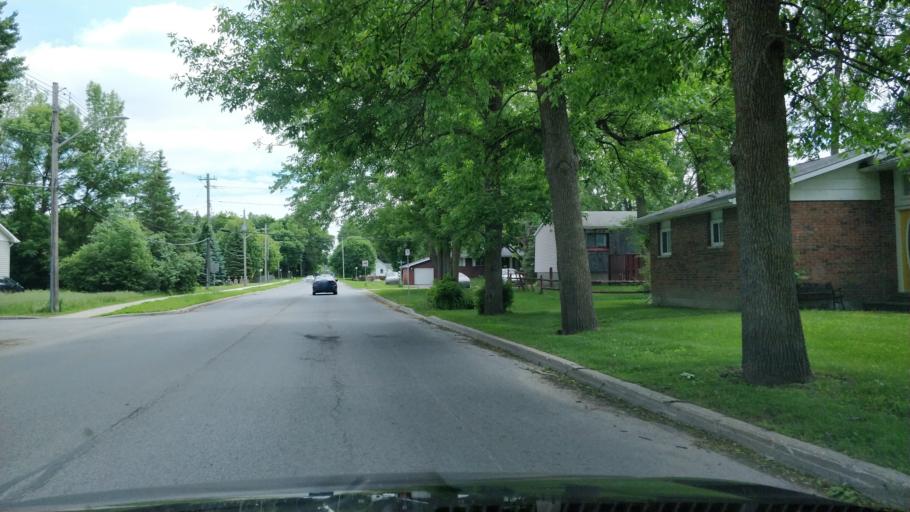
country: CA
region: Ontario
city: Perth
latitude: 44.9102
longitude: -76.2593
